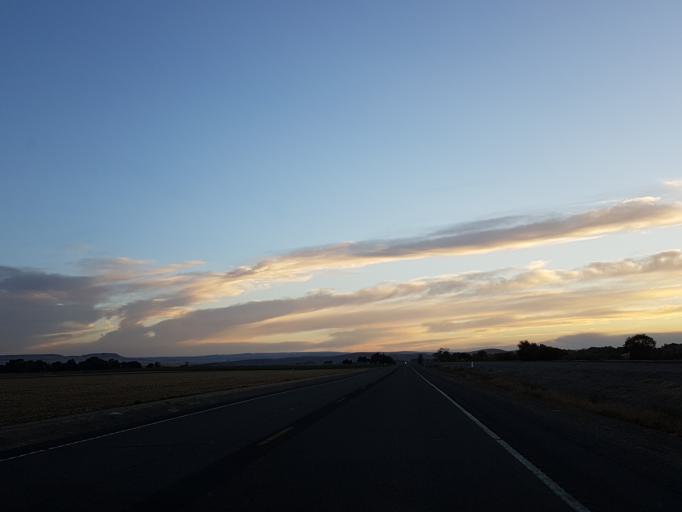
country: US
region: Oregon
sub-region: Malheur County
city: Vale
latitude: 43.9663
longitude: -117.2734
